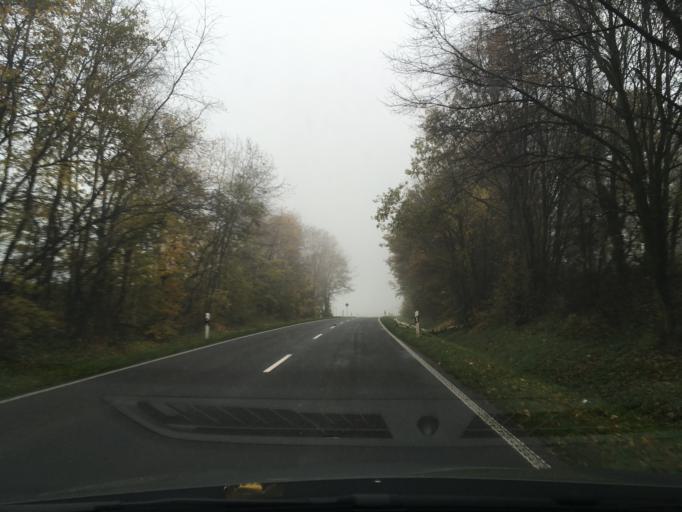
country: DE
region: North Rhine-Westphalia
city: Stadtlohn
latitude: 52.0575
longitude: 6.9397
